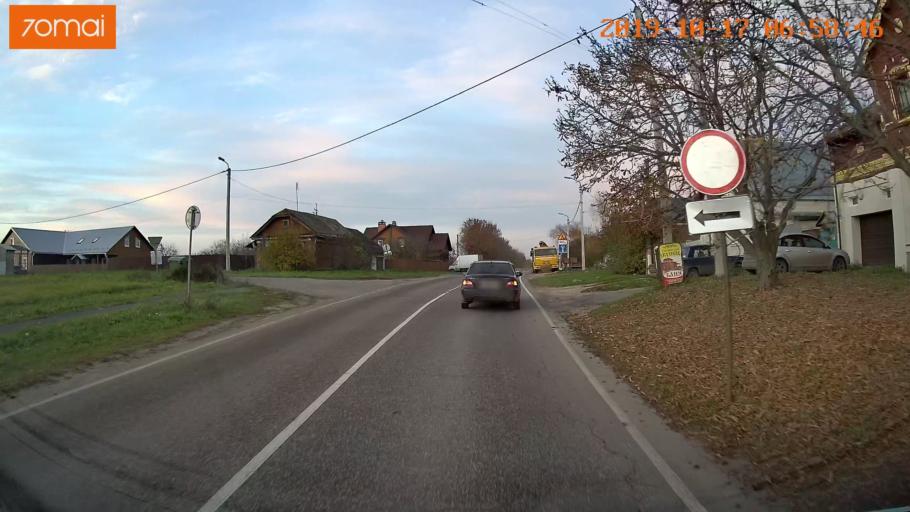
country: RU
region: Vladimir
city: Suzdal'
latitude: 56.4344
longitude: 40.4279
